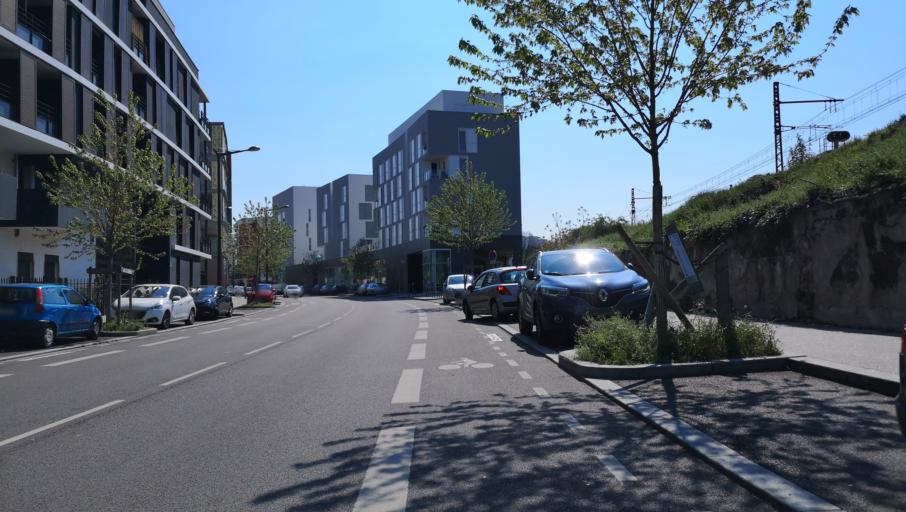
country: FR
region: Rhone-Alpes
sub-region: Departement du Rhone
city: Tassin-la-Demi-Lune
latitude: 45.7774
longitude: 4.8013
